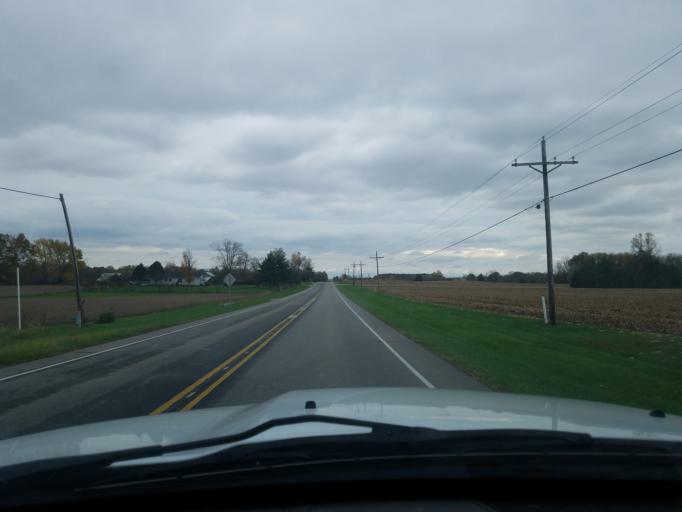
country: US
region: Indiana
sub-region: Bartholomew County
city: Hope
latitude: 39.2636
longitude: -85.7715
